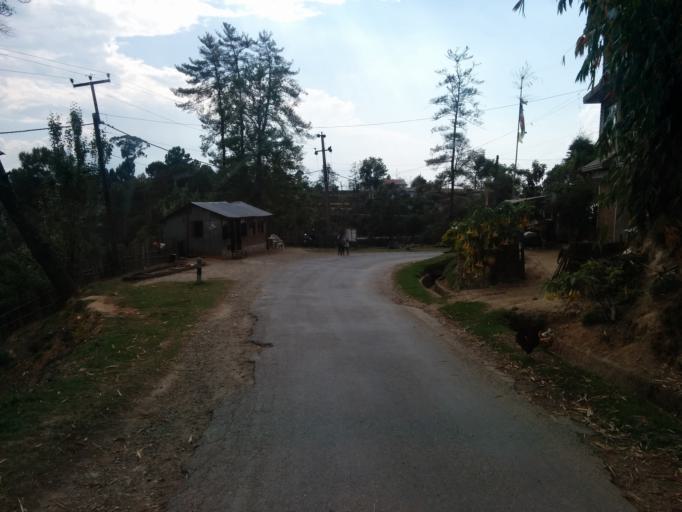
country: NP
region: Central Region
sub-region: Bagmati Zone
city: Nagarkot
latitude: 27.7118
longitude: 85.4919
